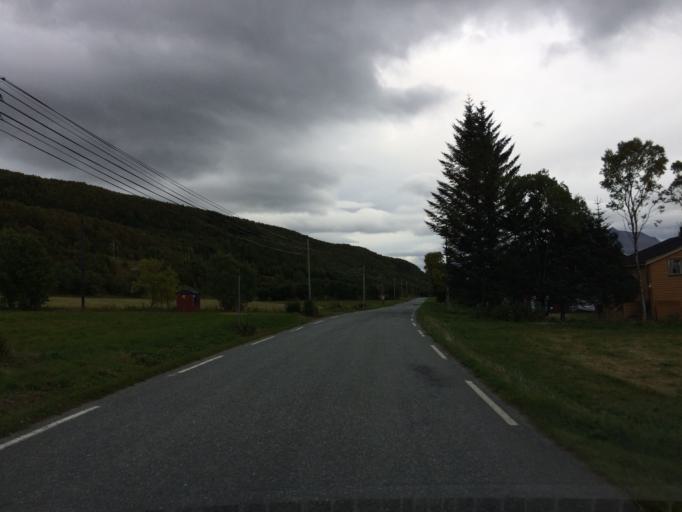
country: NO
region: Troms
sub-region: Sorreisa
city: Sorreisa
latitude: 69.5304
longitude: 18.3061
